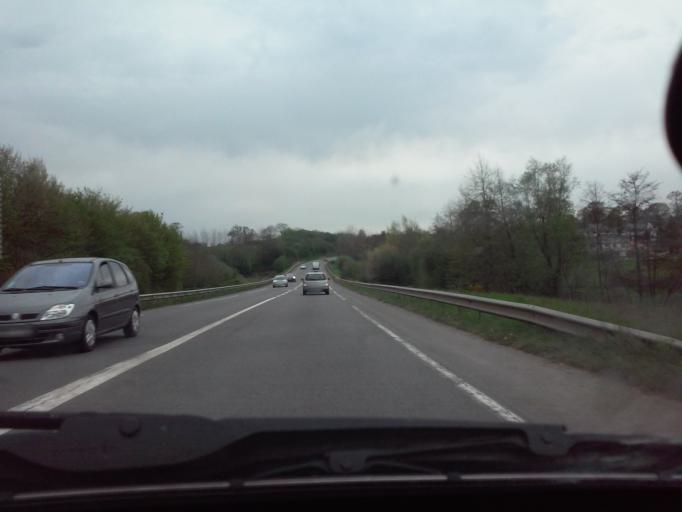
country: FR
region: Brittany
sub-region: Departement d'Ille-et-Vilaine
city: Fougeres
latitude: 48.3392
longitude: -1.2129
